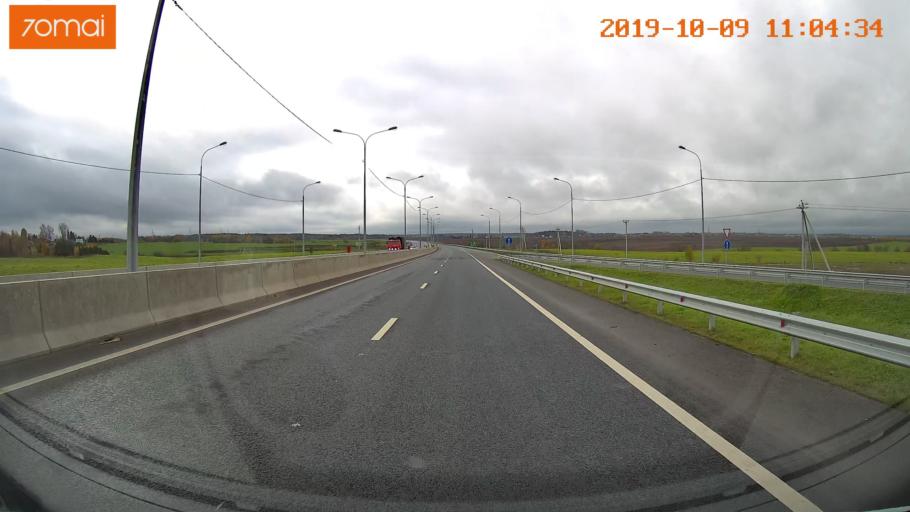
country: RU
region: Vologda
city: Vologda
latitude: 59.2107
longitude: 39.7660
